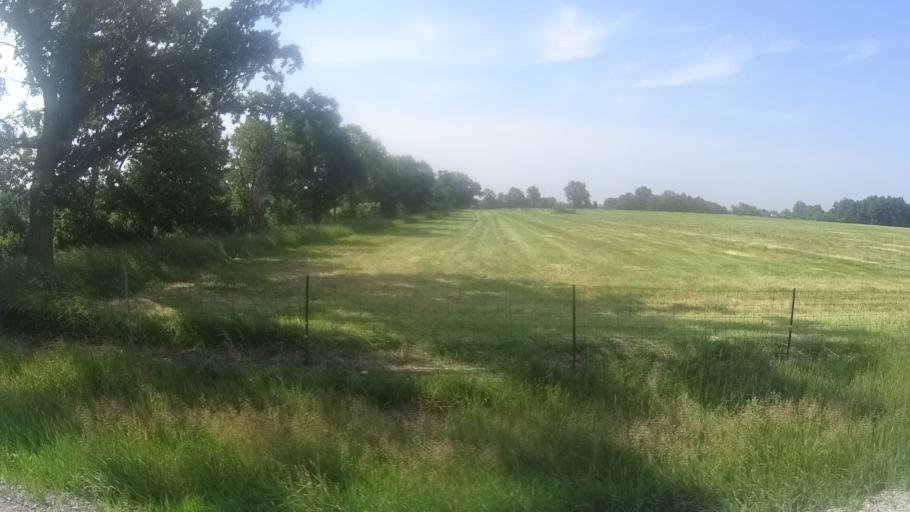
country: US
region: Ohio
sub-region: Huron County
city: Bellevue
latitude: 41.2920
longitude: -82.7641
